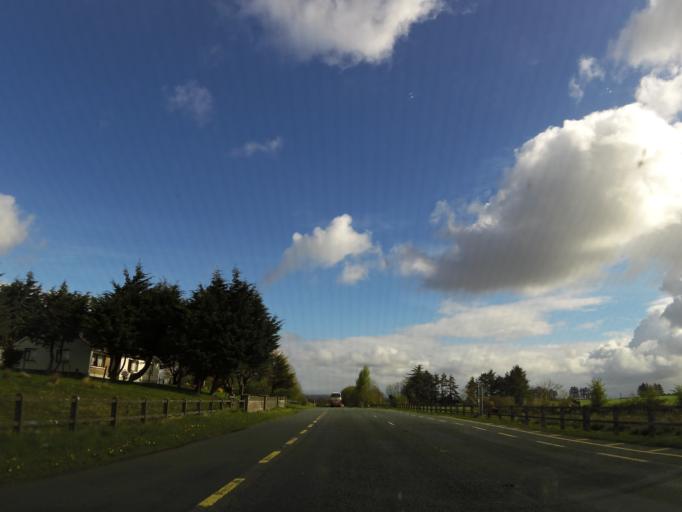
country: IE
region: Connaught
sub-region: Maigh Eo
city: Ballyhaunis
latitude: 53.8376
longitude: -8.8595
